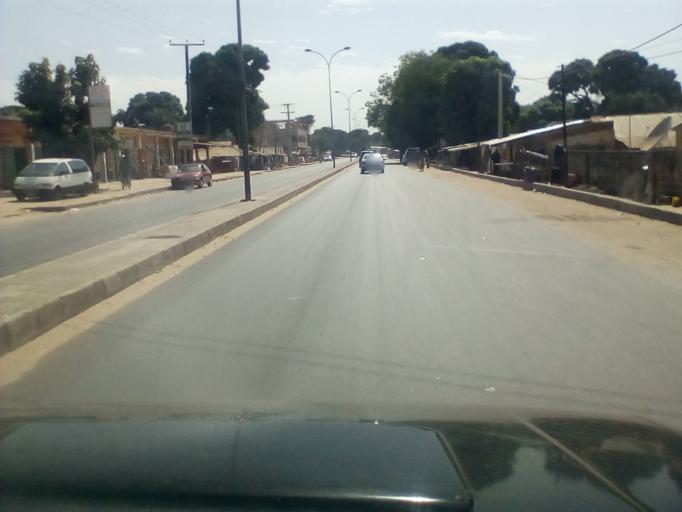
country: GM
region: Western
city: Abuko
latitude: 13.3850
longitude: -16.6434
